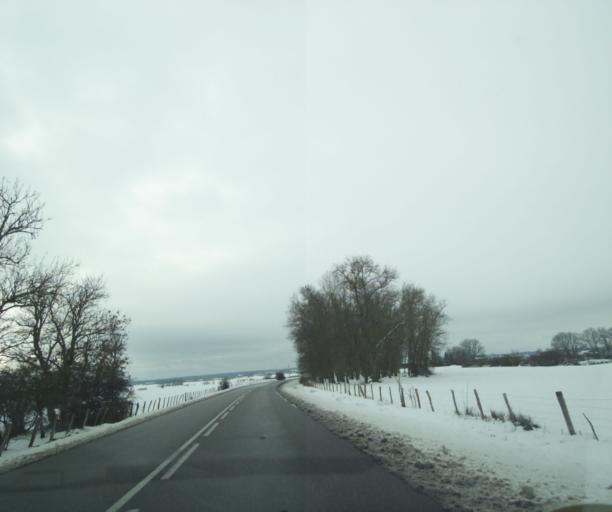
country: FR
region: Champagne-Ardenne
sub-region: Departement de la Haute-Marne
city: Montier-en-Der
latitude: 48.4505
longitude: 4.7395
